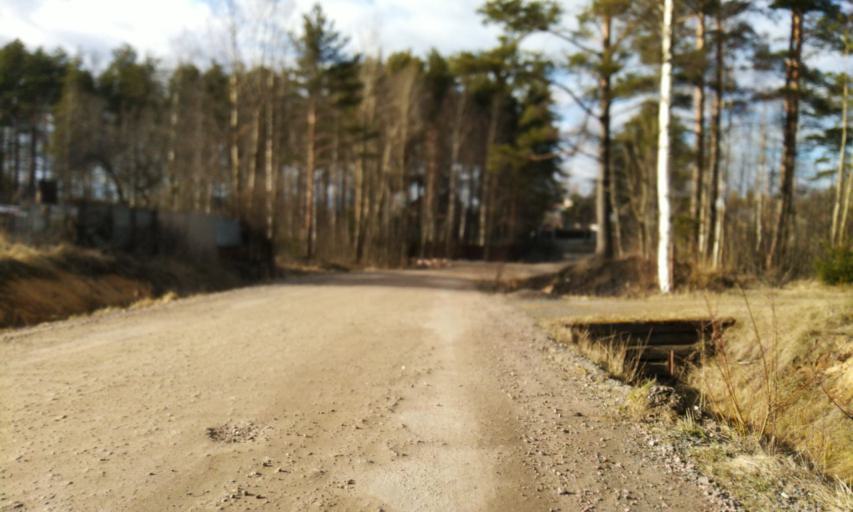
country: RU
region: Leningrad
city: Toksovo
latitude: 60.1196
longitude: 30.4844
